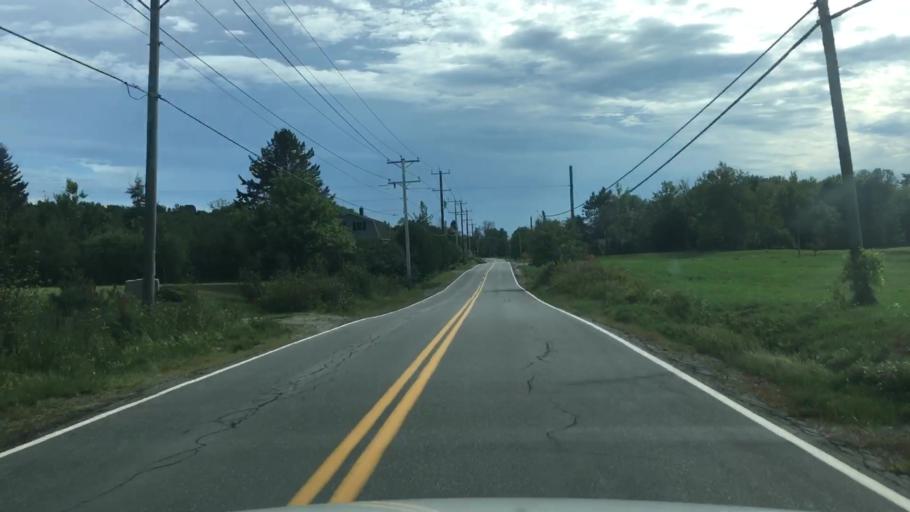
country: US
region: Maine
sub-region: Hancock County
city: Ellsworth
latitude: 44.5036
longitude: -68.4188
